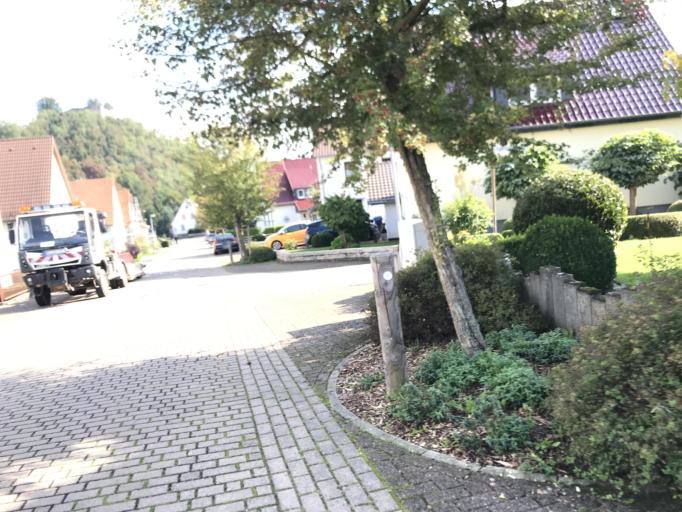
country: DE
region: Hesse
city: Gudensberg
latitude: 51.1758
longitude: 9.3604
